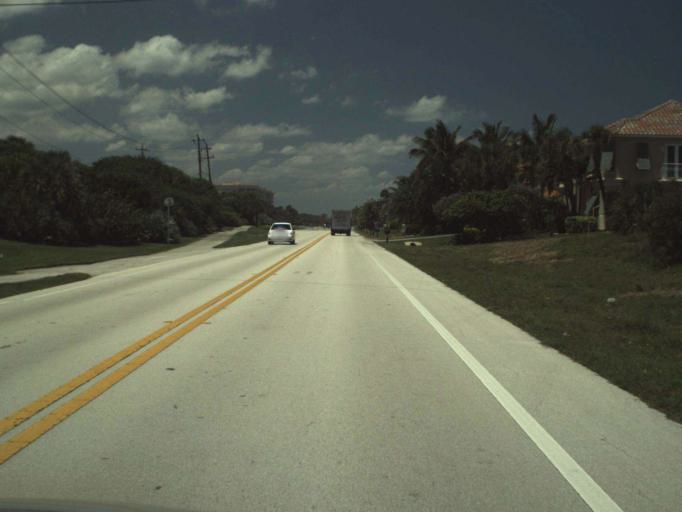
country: US
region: Florida
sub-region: Brevard County
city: Micco
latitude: 27.9193
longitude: -80.4812
